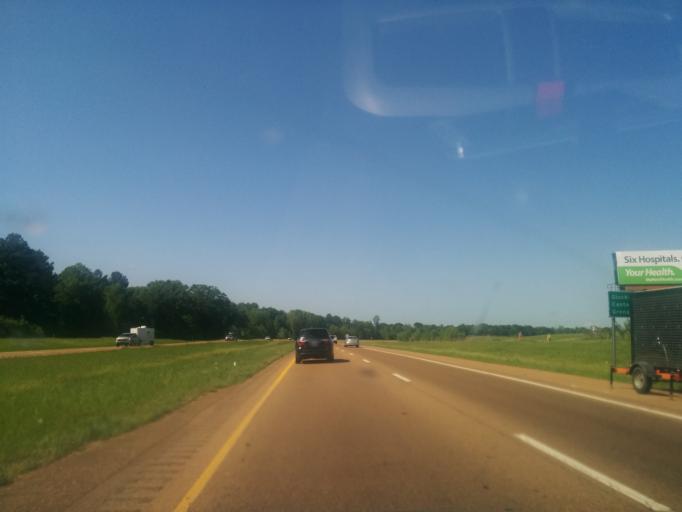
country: US
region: Mississippi
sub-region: Madison County
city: Madison
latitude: 32.4812
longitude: -90.1303
